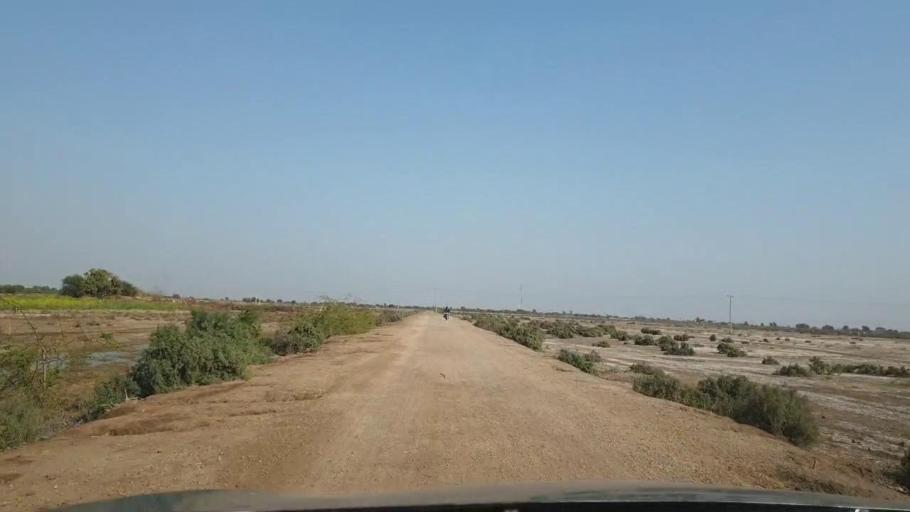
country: PK
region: Sindh
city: Berani
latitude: 25.6223
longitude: 68.8377
